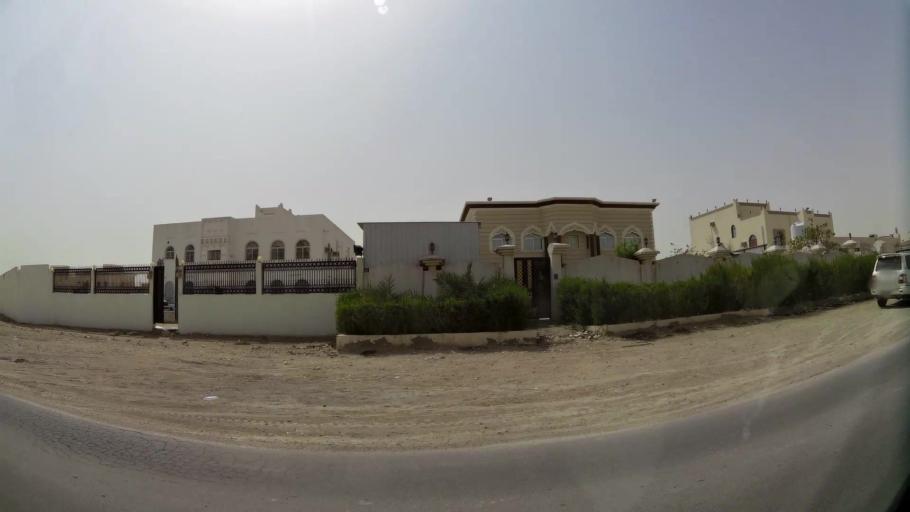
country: QA
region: Baladiyat ar Rayyan
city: Ar Rayyan
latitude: 25.2510
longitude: 51.3721
